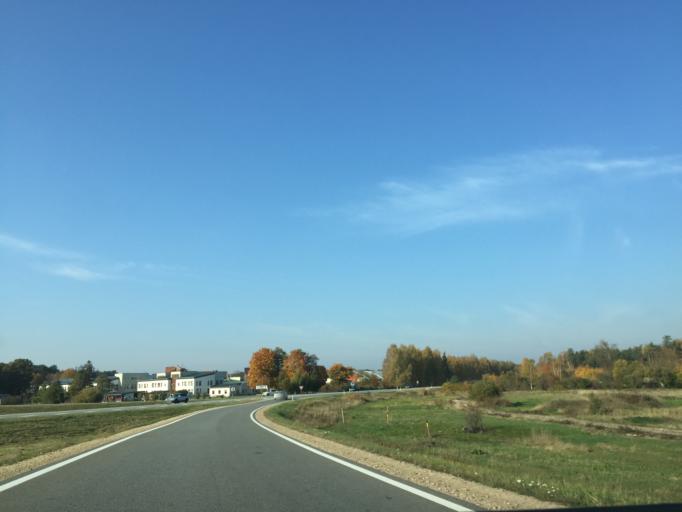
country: LV
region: Babite
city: Pinki
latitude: 56.8786
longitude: 23.9539
